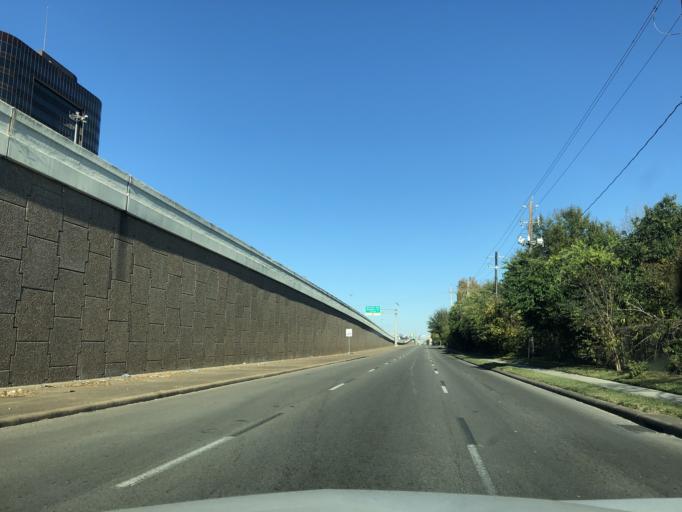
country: US
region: Texas
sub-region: Harris County
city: Bellaire
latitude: 29.7002
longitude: -95.5172
